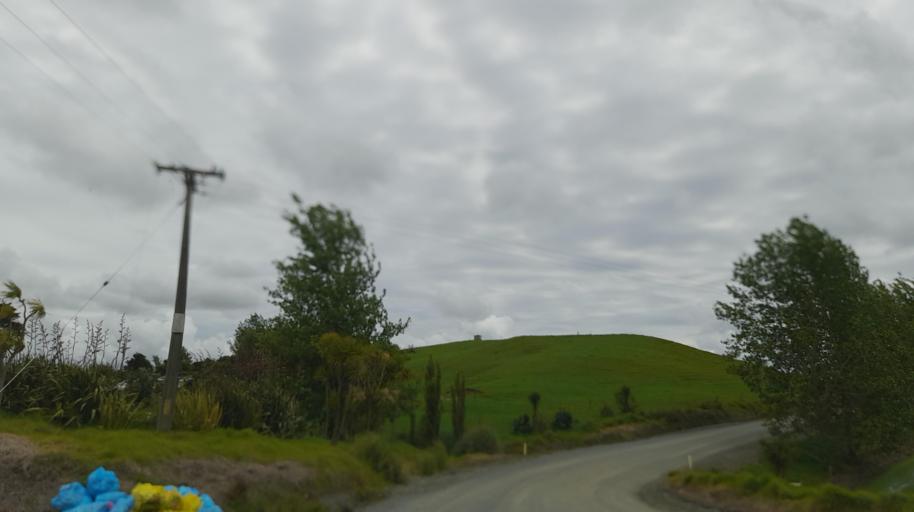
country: NZ
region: Auckland
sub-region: Auckland
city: Wellsford
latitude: -36.2399
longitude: 174.4375
